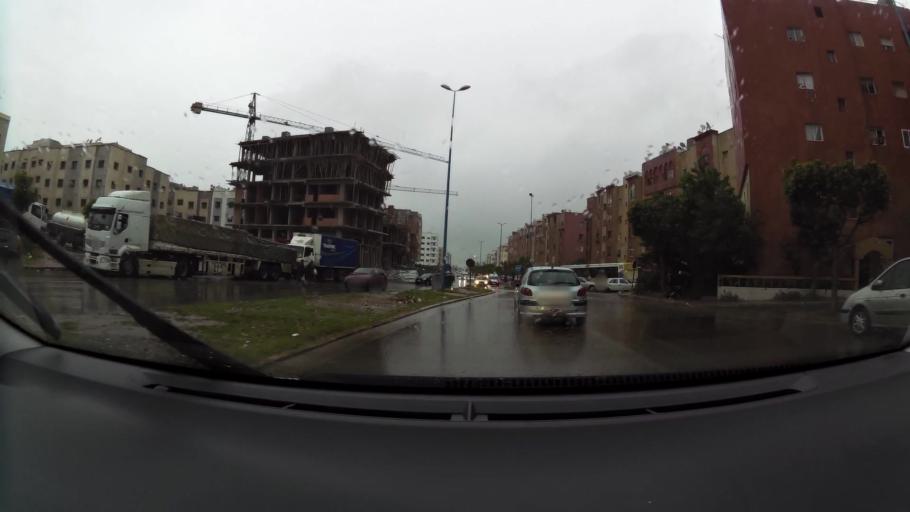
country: MA
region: Grand Casablanca
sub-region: Mediouna
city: Tit Mellil
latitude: 33.5909
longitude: -7.4988
